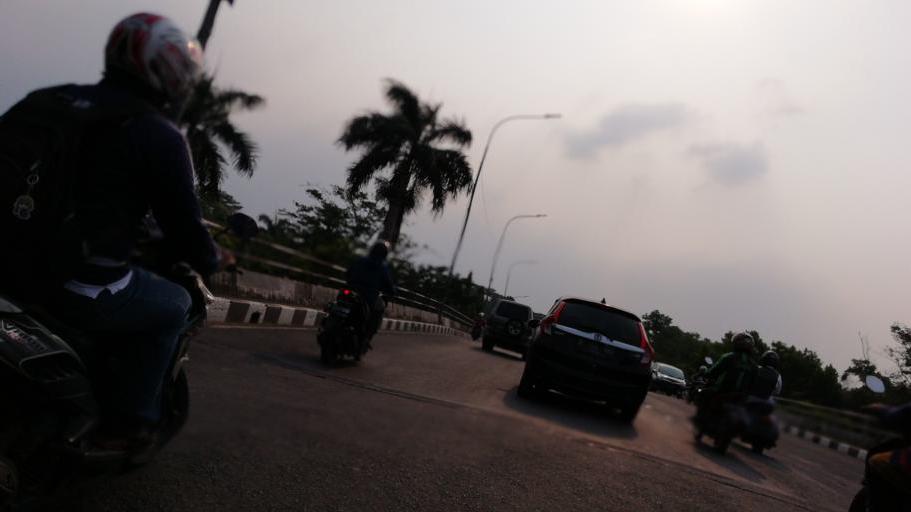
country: ID
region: West Java
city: Depok
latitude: -6.3557
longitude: 106.8322
